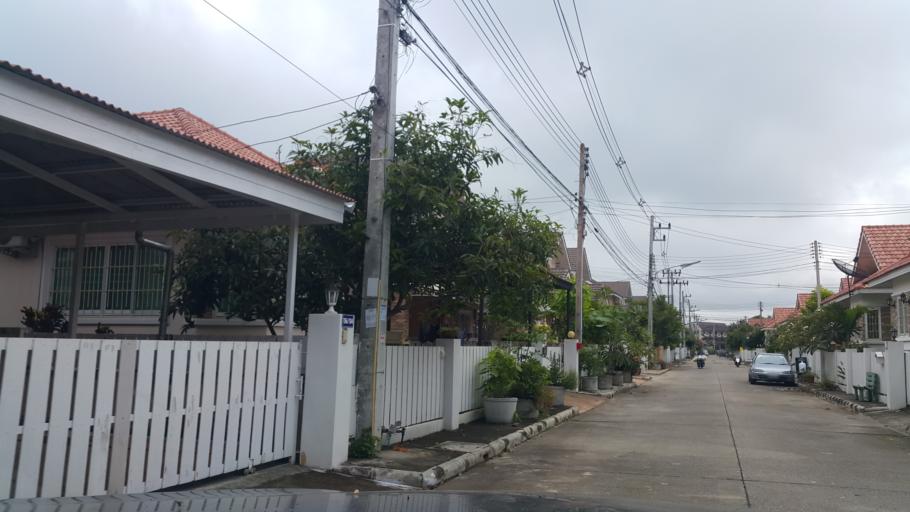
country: TH
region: Chiang Mai
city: San Kamphaeng
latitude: 18.7748
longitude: 99.0839
